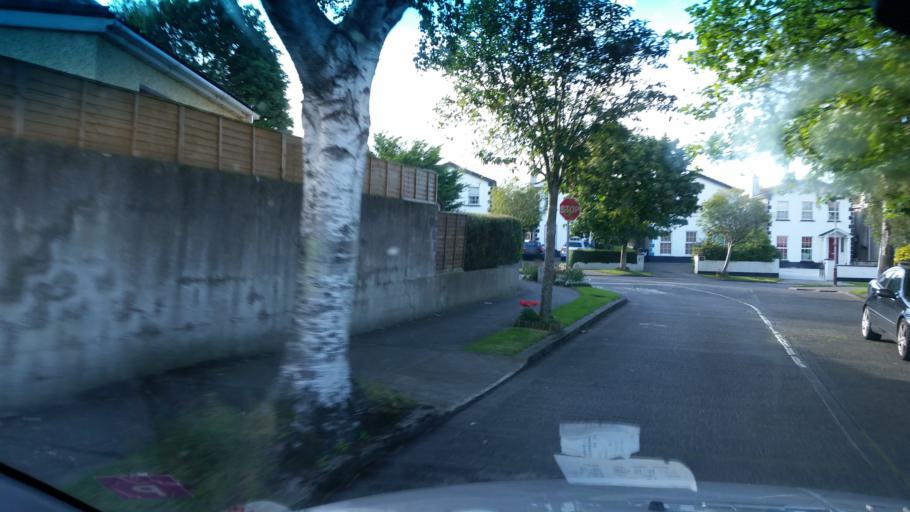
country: IE
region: Leinster
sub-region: Fingal County
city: Blanchardstown
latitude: 53.3855
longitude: -6.3801
